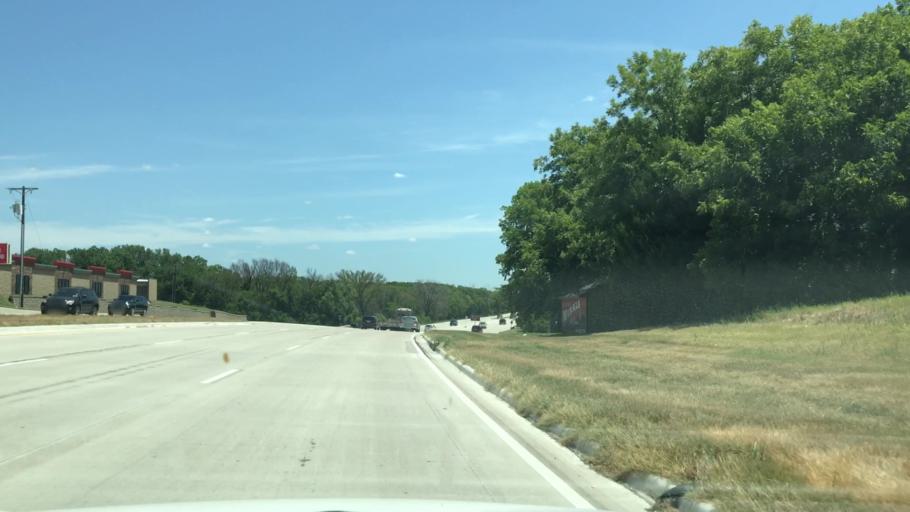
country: US
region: Texas
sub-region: Collin County
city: Lavon
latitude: 33.0260
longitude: -96.4858
